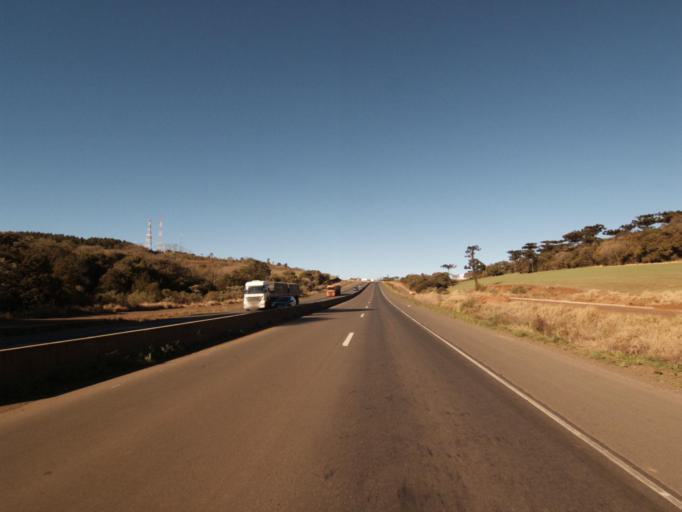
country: BR
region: Santa Catarina
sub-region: Xanxere
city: Xanxere
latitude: -26.8857
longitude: -52.4299
